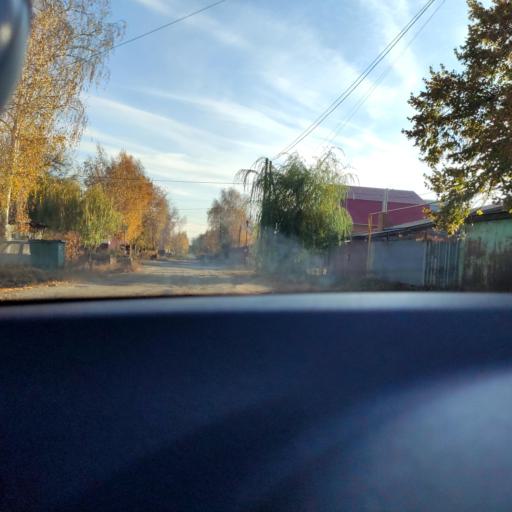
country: RU
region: Samara
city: Petra-Dubrava
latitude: 53.2549
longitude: 50.3242
